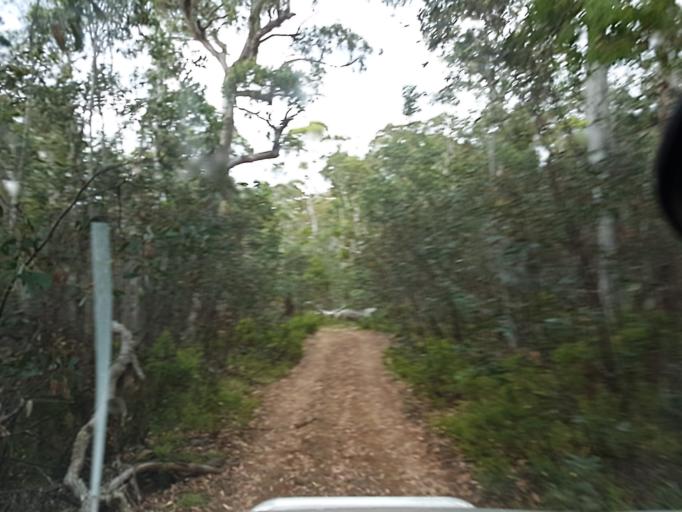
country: AU
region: New South Wales
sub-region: Snowy River
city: Jindabyne
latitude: -36.8763
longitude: 148.1621
